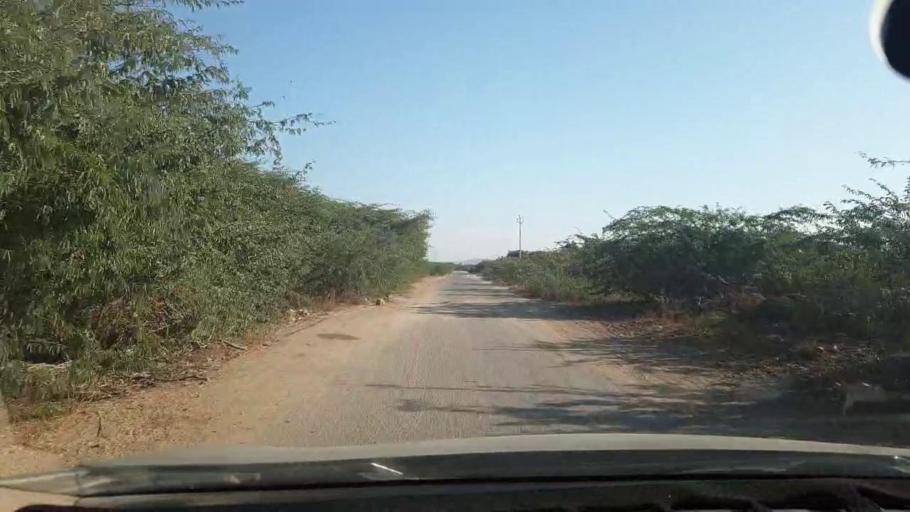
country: PK
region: Sindh
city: Malir Cantonment
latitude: 25.1679
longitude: 67.1979
